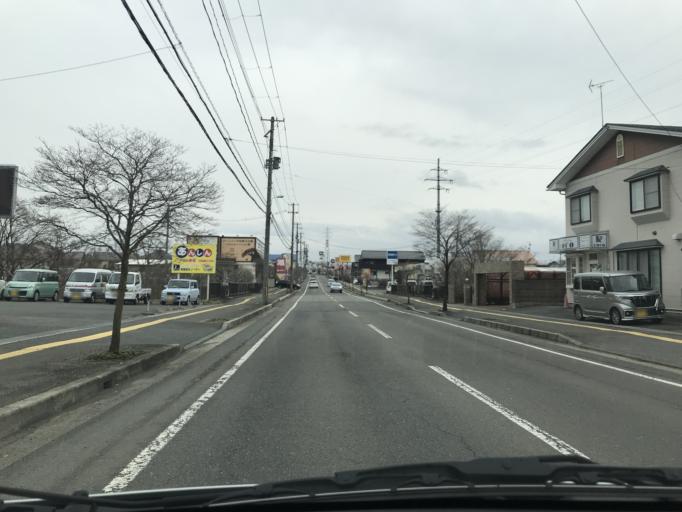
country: JP
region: Iwate
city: Hanamaki
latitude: 39.4044
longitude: 141.1069
